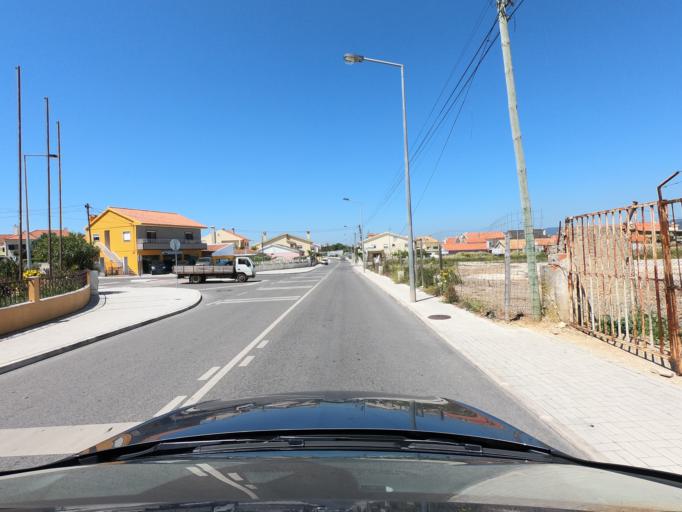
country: PT
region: Lisbon
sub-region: Cascais
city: Parede
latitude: 38.7134
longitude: -9.3577
